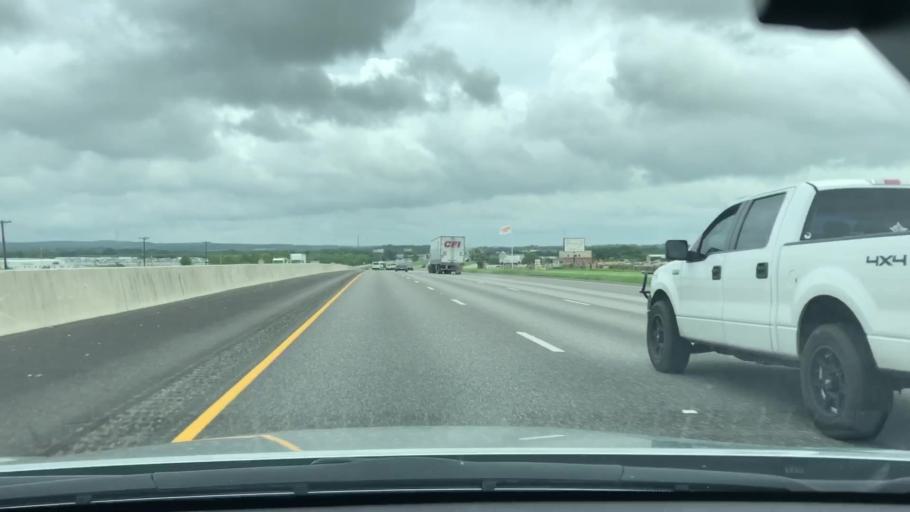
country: US
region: Texas
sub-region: Guadalupe County
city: Lake Dunlap
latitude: 29.7839
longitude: -98.0304
